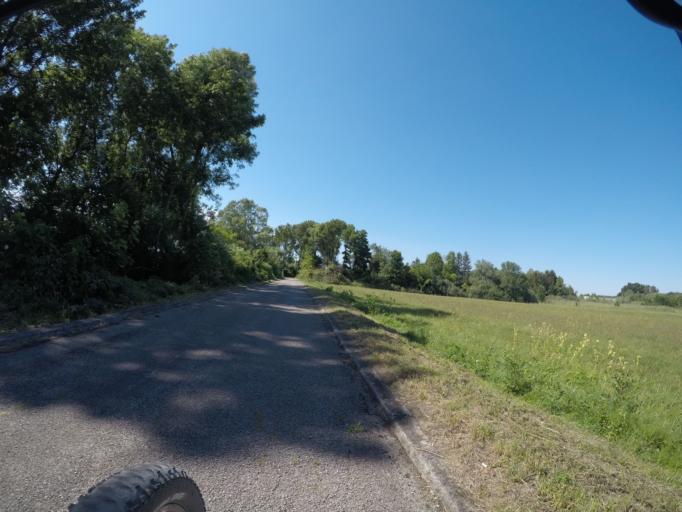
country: AT
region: Lower Austria
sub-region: Politischer Bezirk Wien-Umgebung
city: Moosbrunn
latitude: 48.0091
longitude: 16.4573
